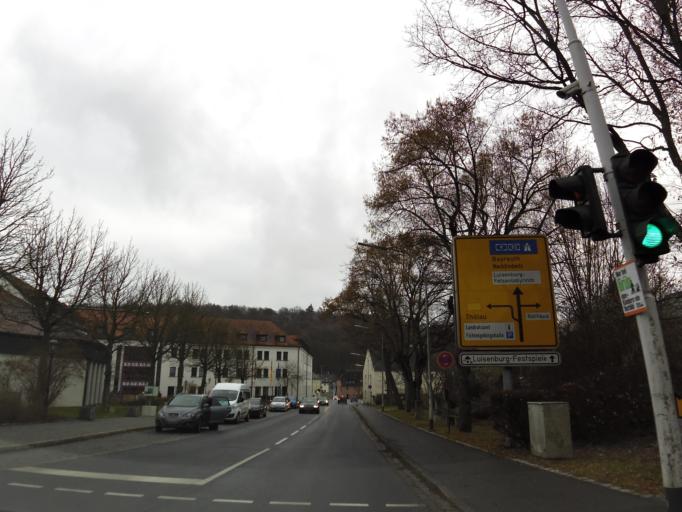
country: DE
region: Bavaria
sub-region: Upper Franconia
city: Wunsiedel
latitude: 50.0383
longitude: 12.0052
